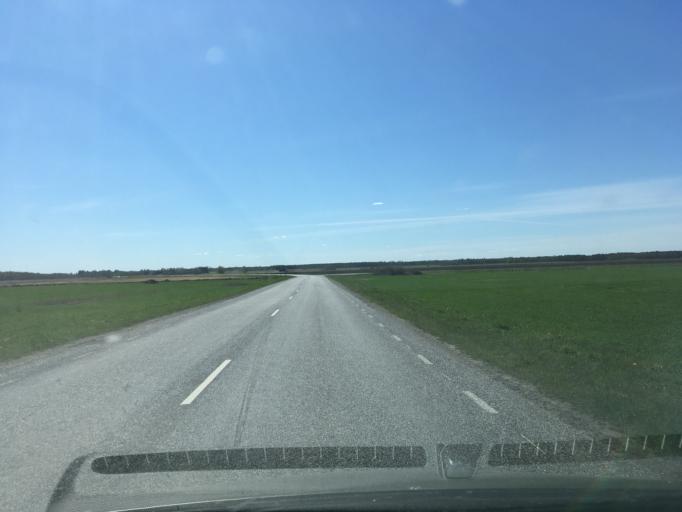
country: EE
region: Harju
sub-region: Raasiku vald
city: Arukula
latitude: 59.4275
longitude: 25.0788
